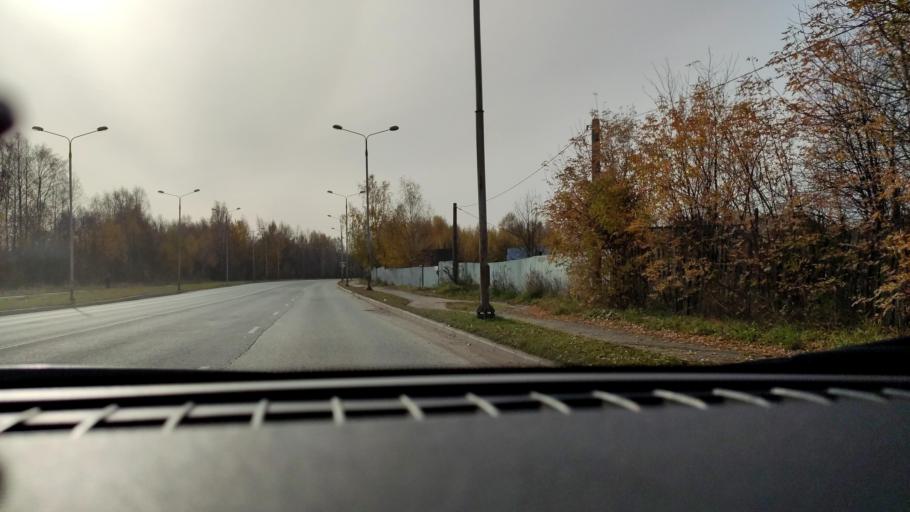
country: RU
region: Perm
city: Polazna
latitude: 58.1127
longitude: 56.3999
